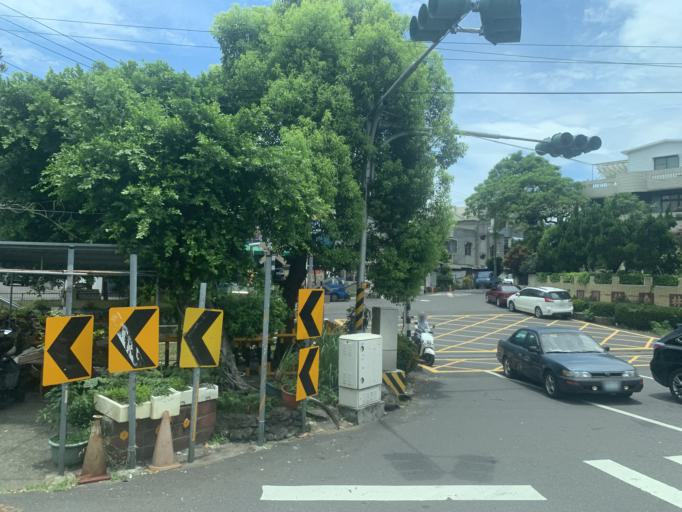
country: TW
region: Taiwan
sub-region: Chiayi
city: Jiayi Shi
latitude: 23.4921
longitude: 120.4705
